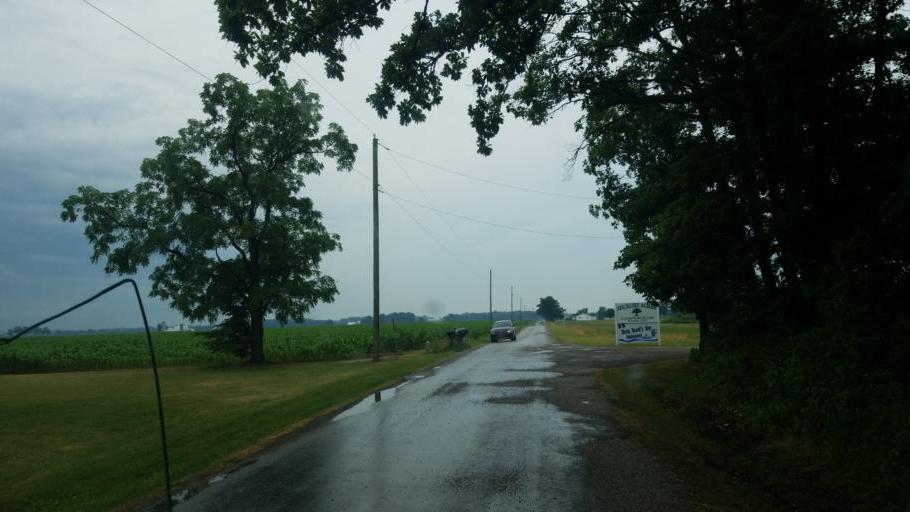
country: US
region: Ohio
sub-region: Williams County
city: Edgerton
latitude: 41.4233
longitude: -84.6704
